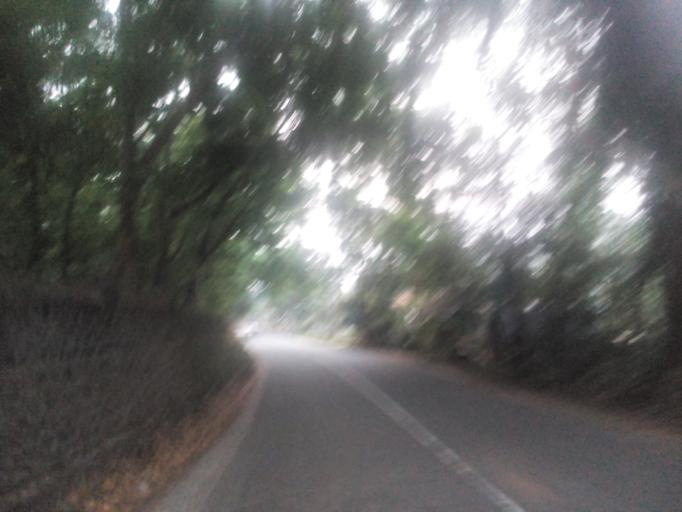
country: IN
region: Kerala
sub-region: Kottayam
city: Palackattumala
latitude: 9.8073
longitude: 76.6652
